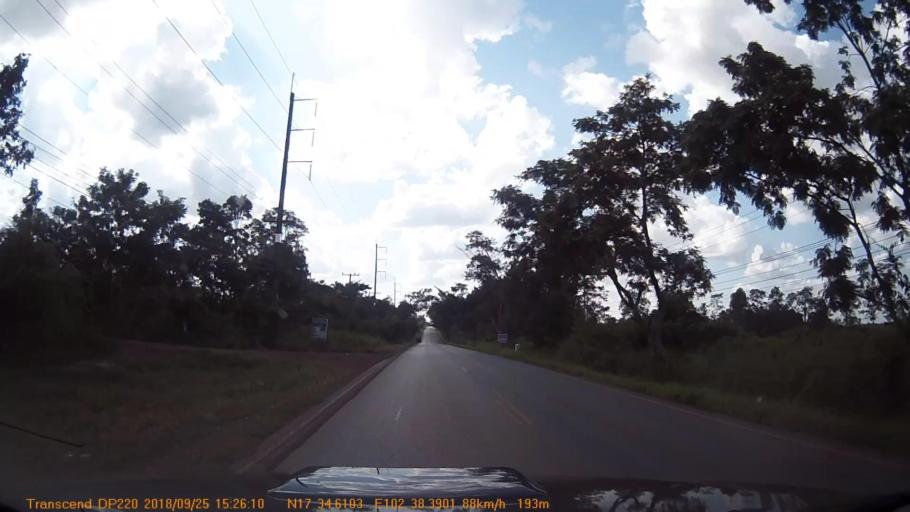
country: TH
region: Nong Khai
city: Sa Khrai
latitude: 17.5769
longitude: 102.6396
